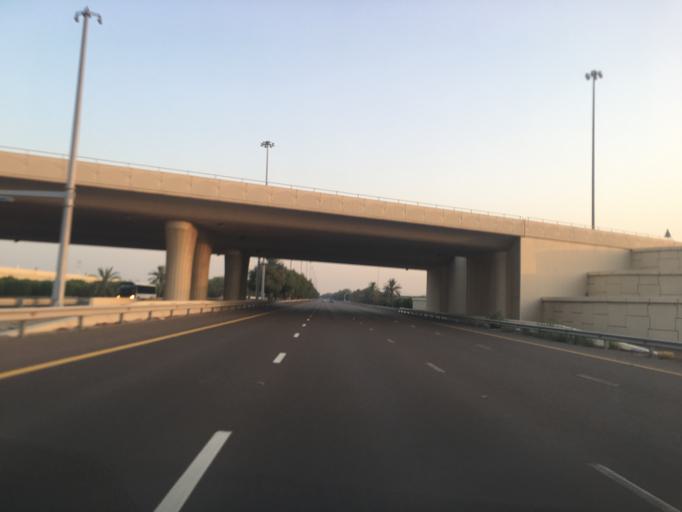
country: AE
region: Abu Dhabi
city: Abu Dhabi
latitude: 24.3516
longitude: 54.5696
